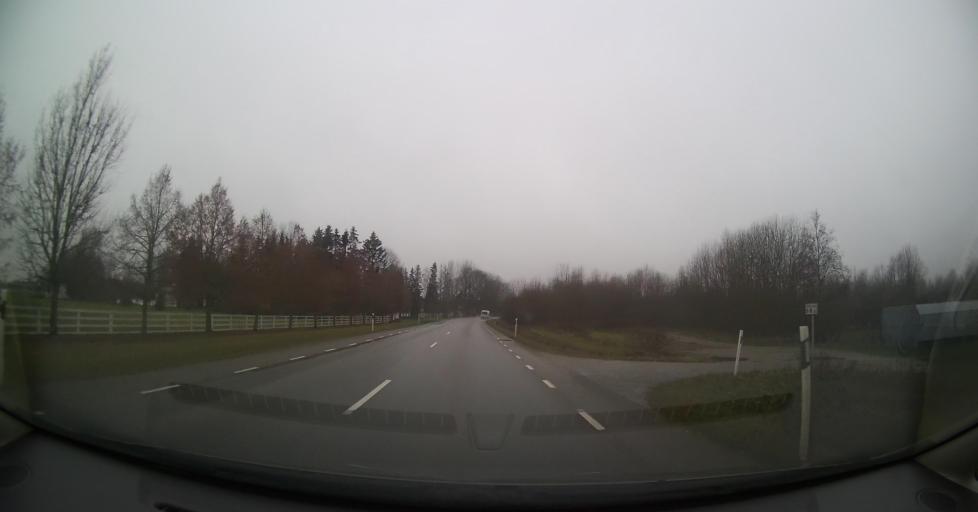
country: EE
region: Tartu
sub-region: Tartu linn
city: Tartu
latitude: 58.3873
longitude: 26.7903
